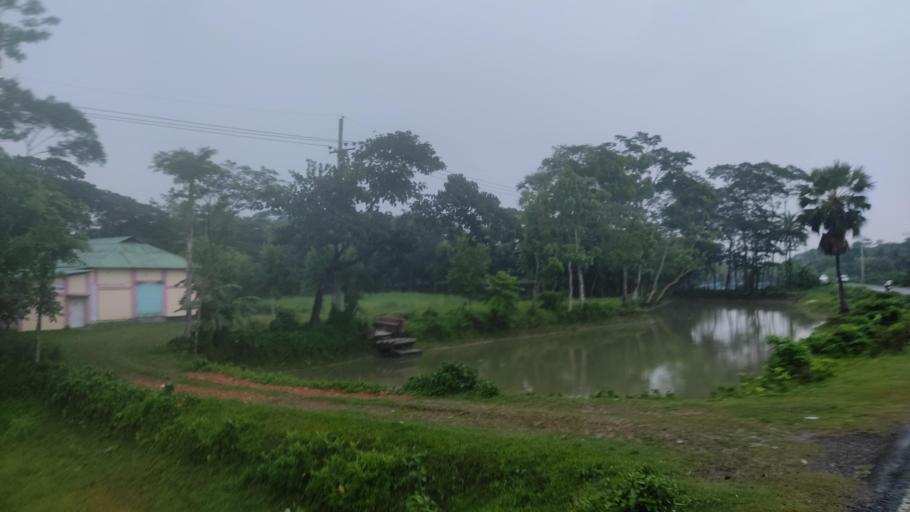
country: BD
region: Barisal
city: Bhandaria
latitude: 22.3008
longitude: 90.3242
